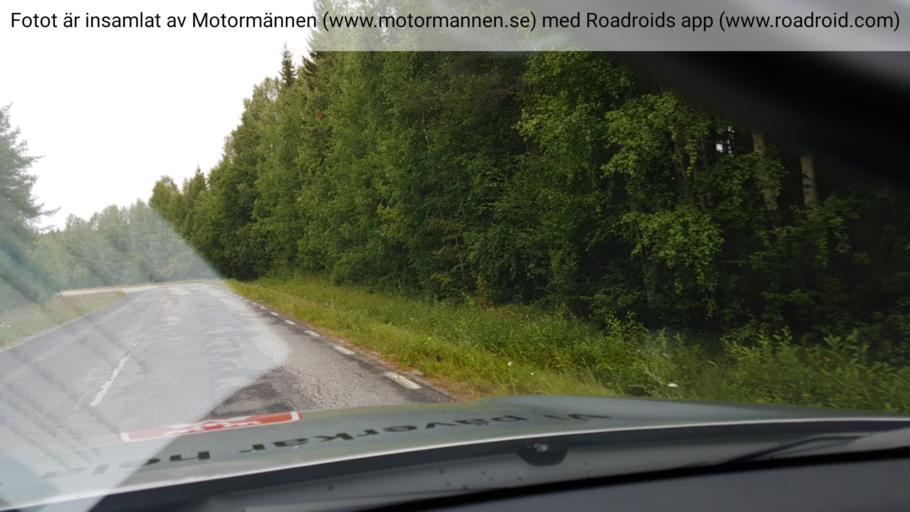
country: SE
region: Norrbotten
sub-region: Bodens Kommun
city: Saevast
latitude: 65.6688
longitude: 21.7387
